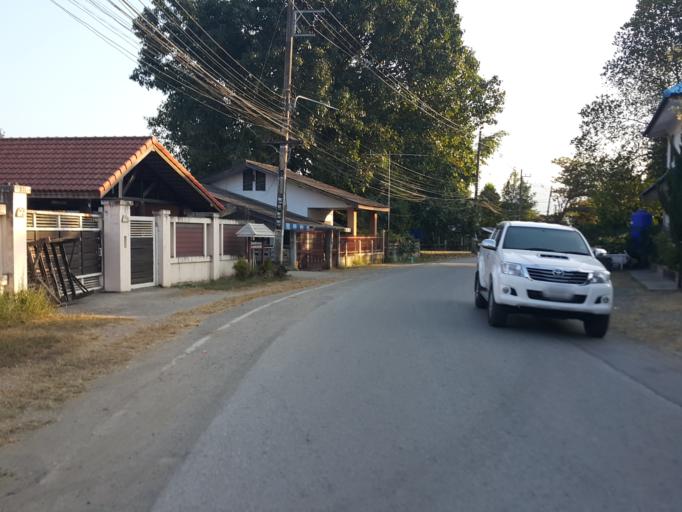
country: TH
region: Chiang Mai
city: Mae On
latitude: 18.7852
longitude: 99.2575
